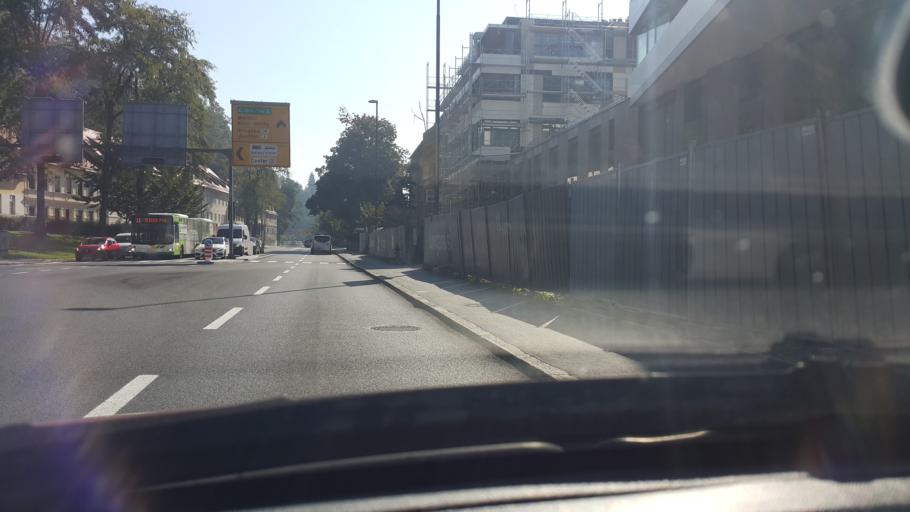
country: SI
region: Ljubljana
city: Ljubljana
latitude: 46.0449
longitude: 14.5088
